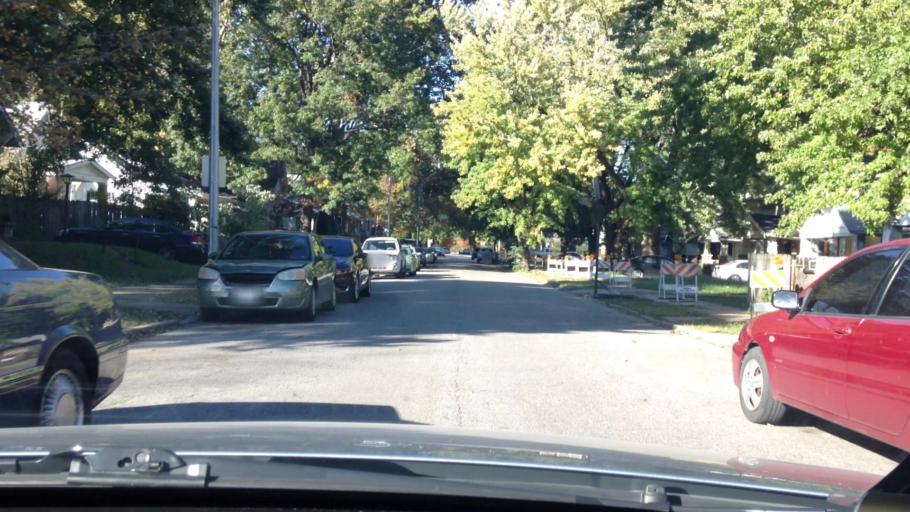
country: US
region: Kansas
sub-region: Johnson County
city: Mission Hills
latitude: 39.0255
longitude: -94.5704
